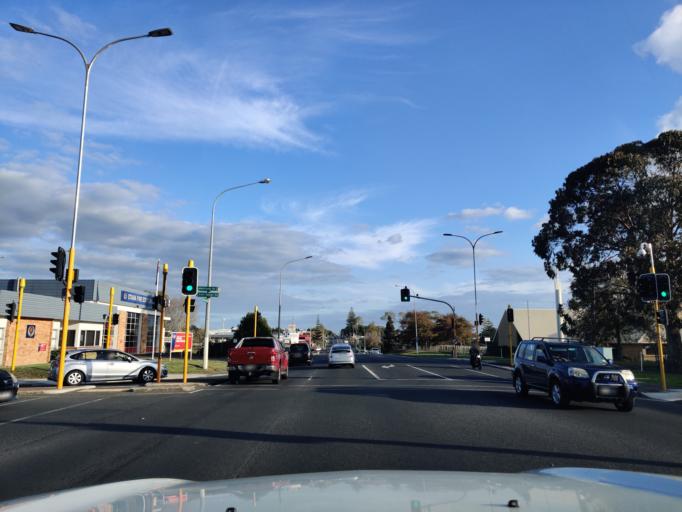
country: NZ
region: Auckland
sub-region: Auckland
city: Manukau City
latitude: -36.9538
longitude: 174.8909
